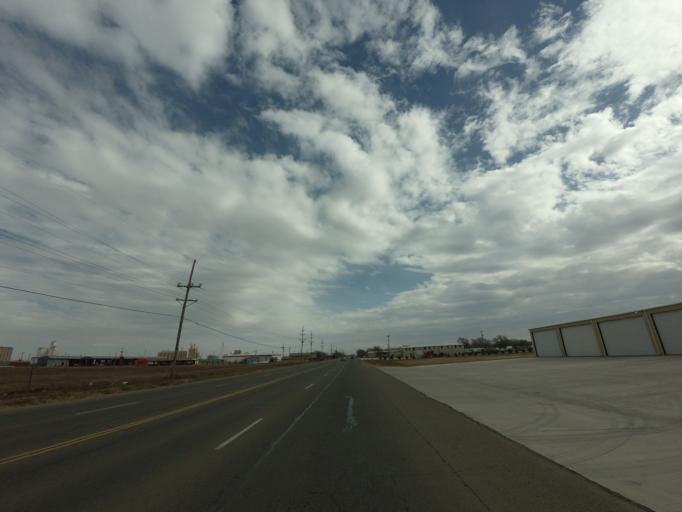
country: US
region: New Mexico
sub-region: Curry County
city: Clovis
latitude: 34.3902
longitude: -103.2067
